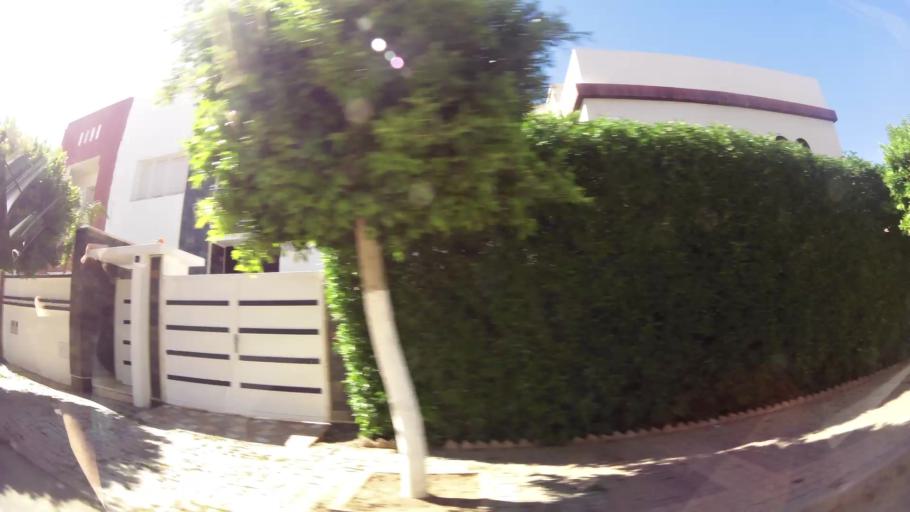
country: MA
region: Oriental
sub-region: Oujda-Angad
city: Oujda
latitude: 34.7202
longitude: -1.9118
